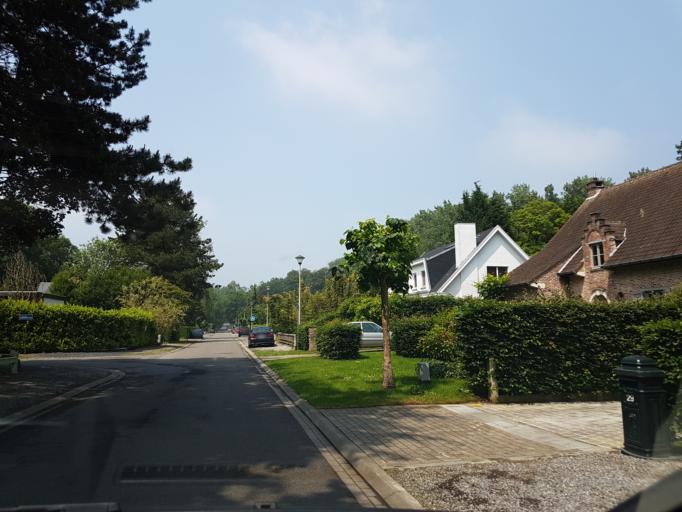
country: BE
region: Flanders
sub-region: Provincie Vlaams-Brabant
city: Steenokkerzeel
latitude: 50.9287
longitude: 4.5182
